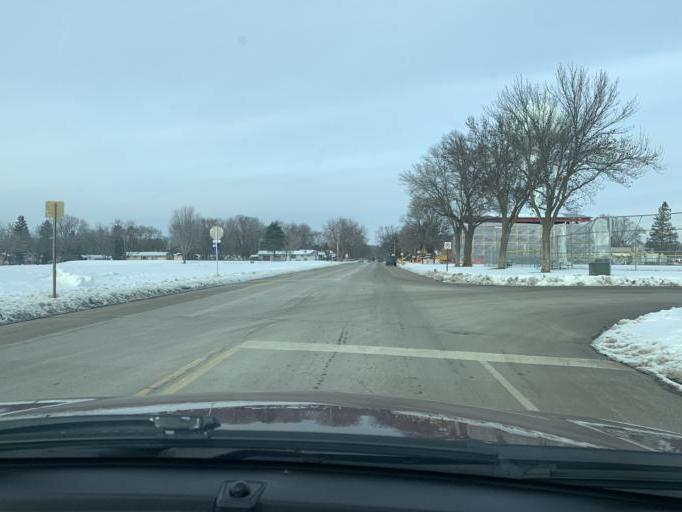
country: US
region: Minnesota
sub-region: Washington County
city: Saint Paul Park
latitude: 44.8332
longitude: -92.9841
